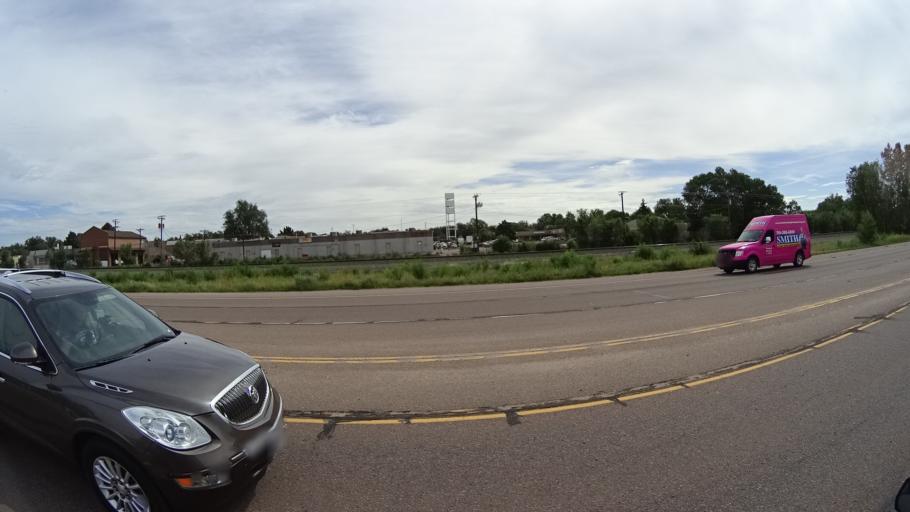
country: US
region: Colorado
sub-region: El Paso County
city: Security-Widefield
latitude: 38.7344
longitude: -104.7288
